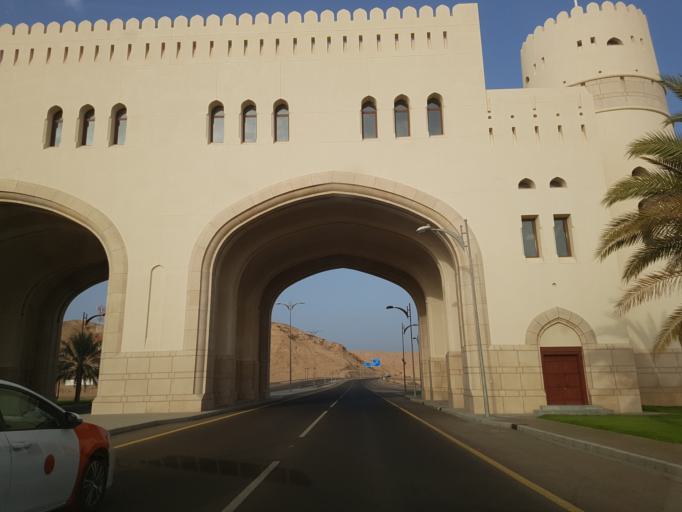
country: OM
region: Al Buraimi
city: Al Buraymi
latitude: 24.2331
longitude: 55.9355
